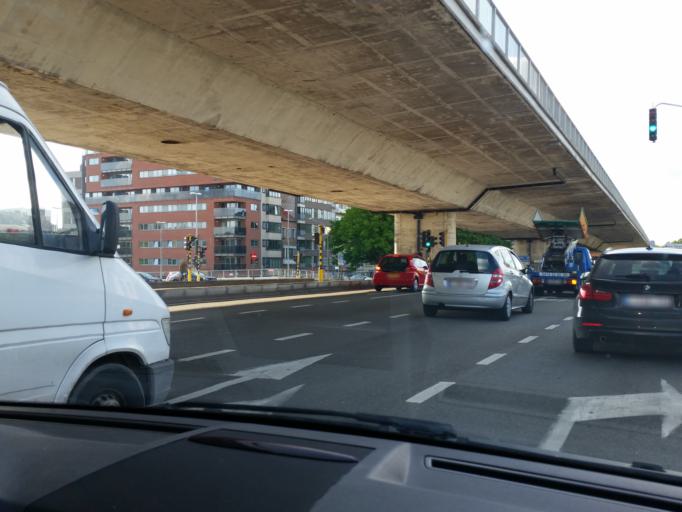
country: BE
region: Flanders
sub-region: Provincie Oost-Vlaanderen
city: Ledeberg
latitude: 51.0382
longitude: 3.7370
